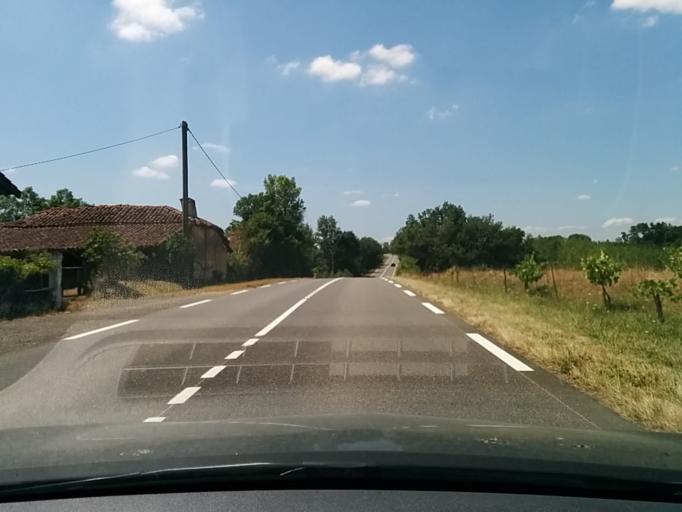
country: FR
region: Midi-Pyrenees
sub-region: Departement du Gers
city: Eauze
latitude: 43.7932
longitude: 0.0885
